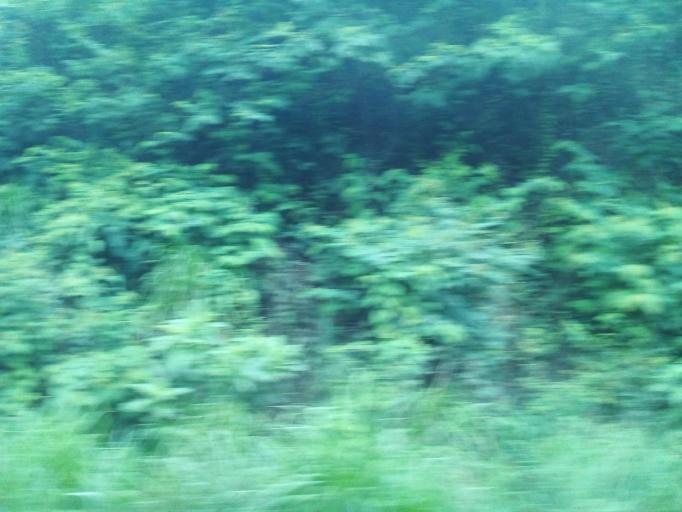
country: BR
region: Minas Gerais
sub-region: Joao Monlevade
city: Joao Monlevade
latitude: -19.8255
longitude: -43.1176
